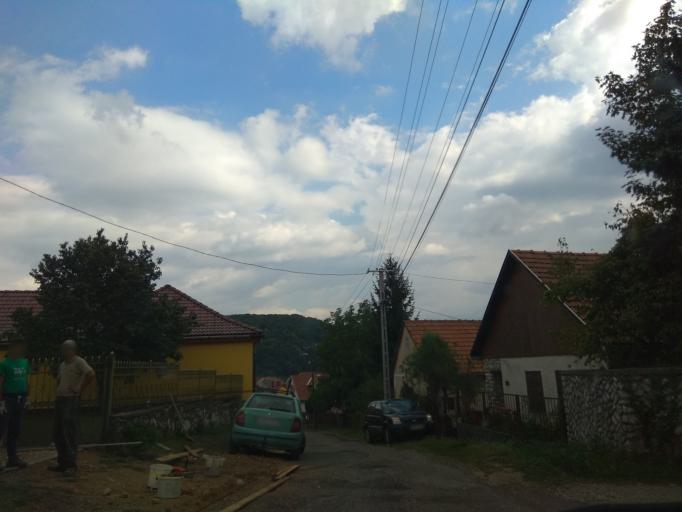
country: HU
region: Borsod-Abauj-Zemplen
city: Saly
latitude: 48.0692
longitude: 20.6294
